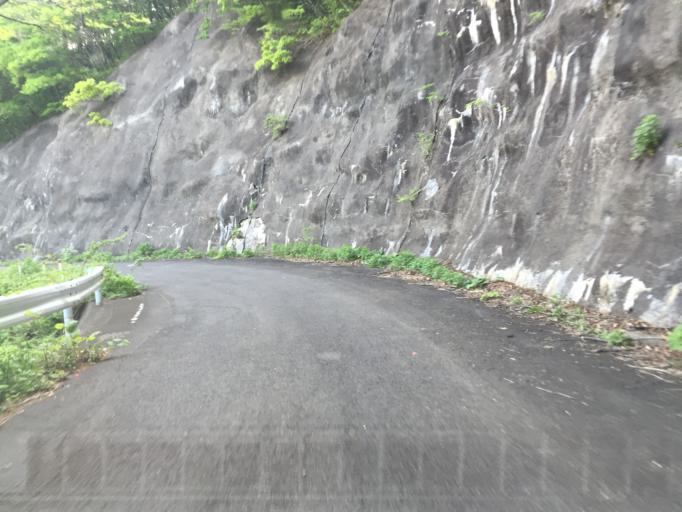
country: JP
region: Fukushima
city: Yanagawamachi-saiwaicho
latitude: 37.8504
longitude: 140.6810
